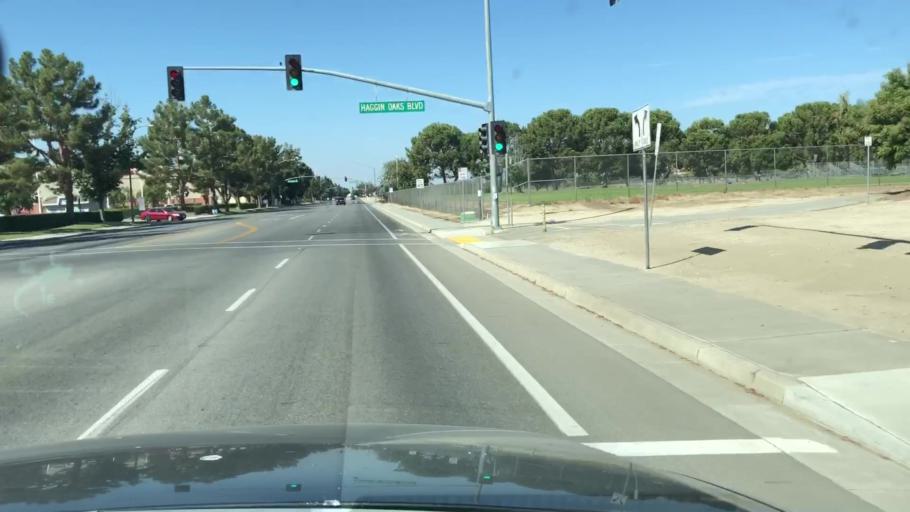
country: US
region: California
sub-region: Kern County
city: Greenacres
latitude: 35.3430
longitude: -119.1010
